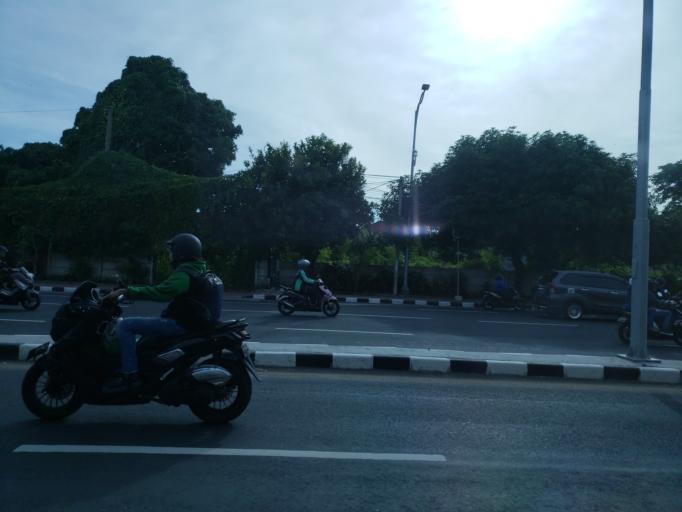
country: ID
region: Bali
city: Kelanabian
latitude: -8.7428
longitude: 115.1820
